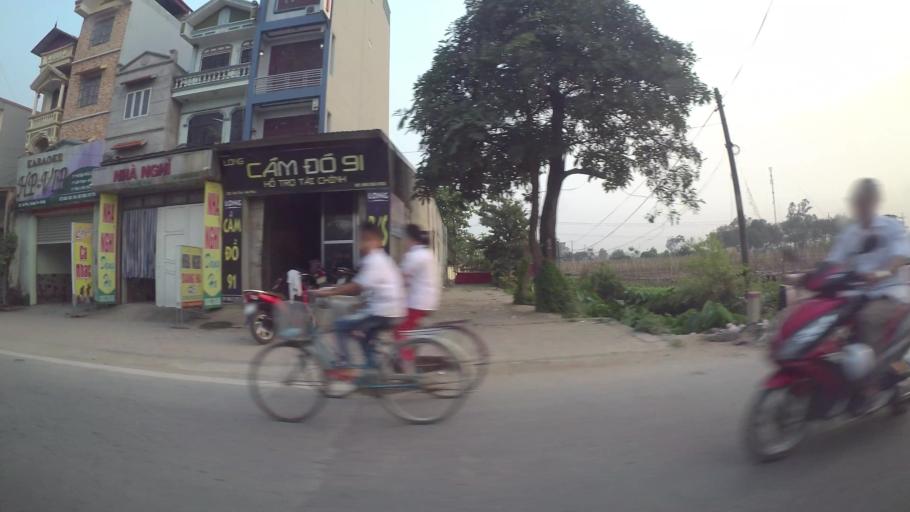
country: VN
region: Ha Noi
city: Thuong Tin
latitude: 20.8677
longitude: 105.8528
